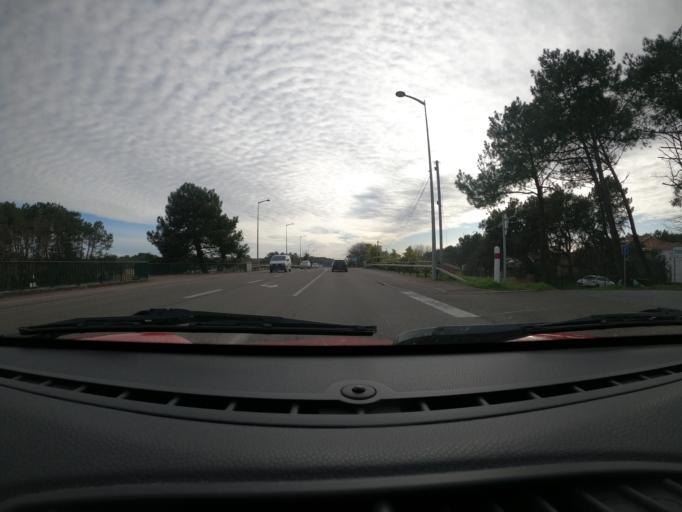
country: FR
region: Aquitaine
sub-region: Departement des Landes
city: Labenne
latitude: 43.5860
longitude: -1.4303
